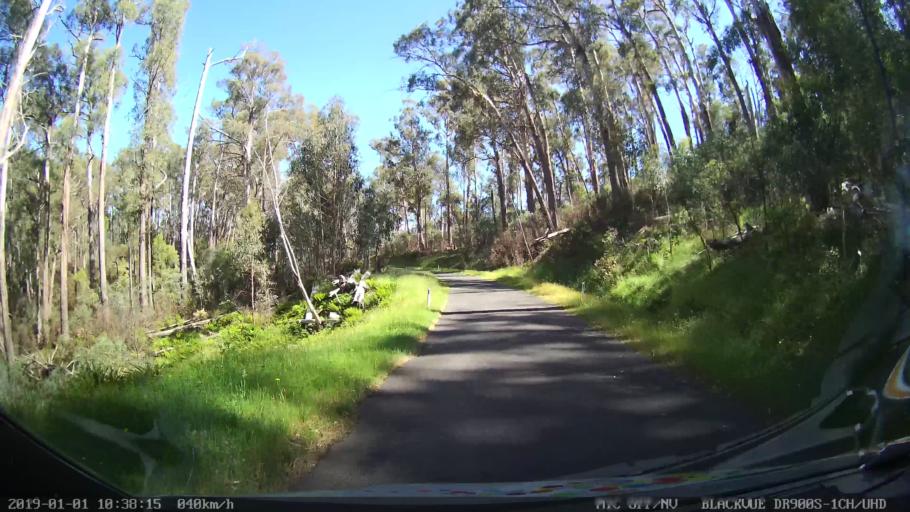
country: AU
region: New South Wales
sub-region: Snowy River
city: Jindabyne
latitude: -36.0463
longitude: 148.3015
